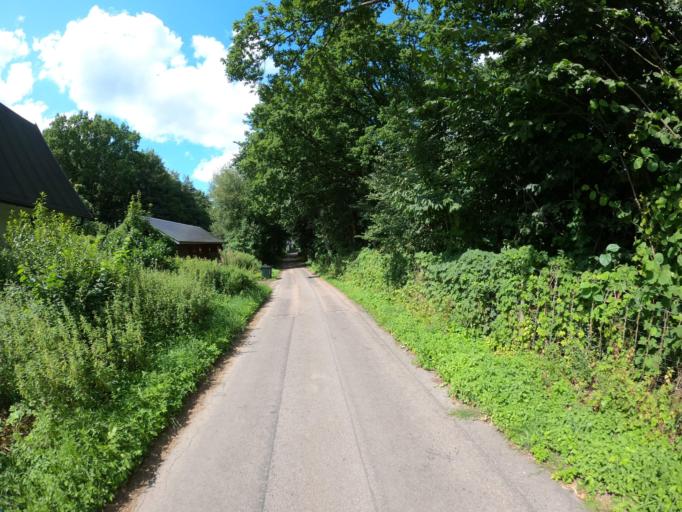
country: SE
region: Skane
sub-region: Lunds Kommun
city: Veberod
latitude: 55.5888
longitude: 13.4891
